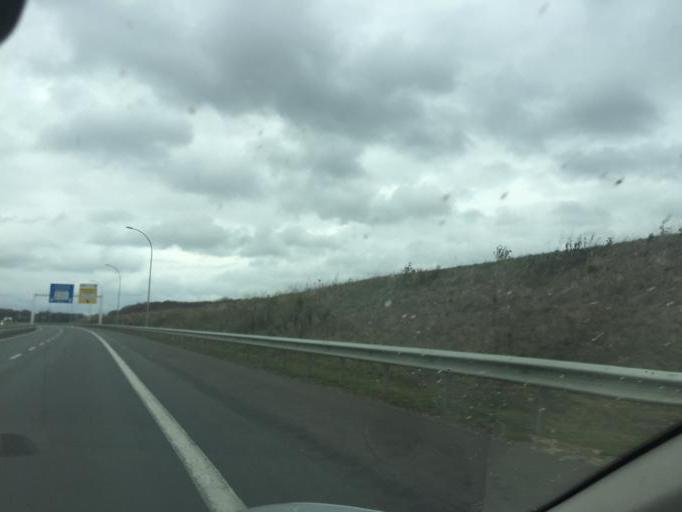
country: LU
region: Luxembourg
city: Crauthem
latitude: 49.5024
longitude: 6.1400
